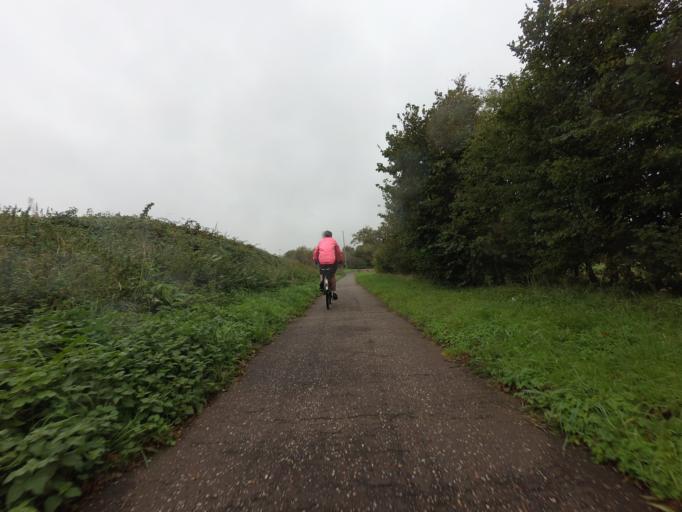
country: GB
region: England
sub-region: Norfolk
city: Dersingham
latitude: 52.8040
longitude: 0.4847
